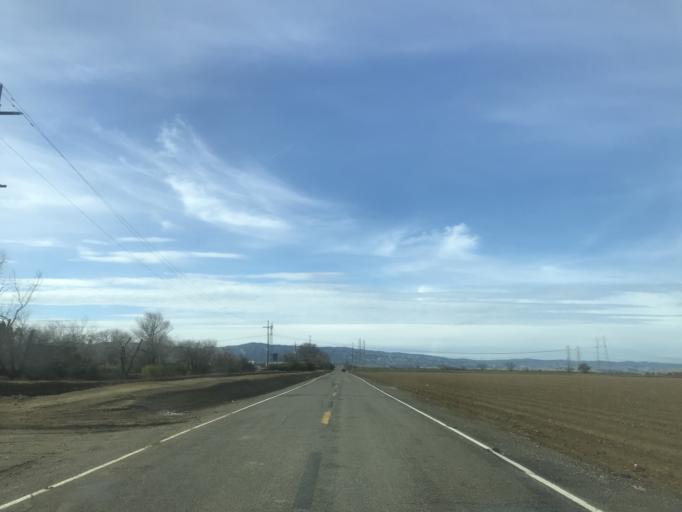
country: US
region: California
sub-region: Yolo County
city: Cottonwood
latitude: 38.6638
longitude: -121.9380
